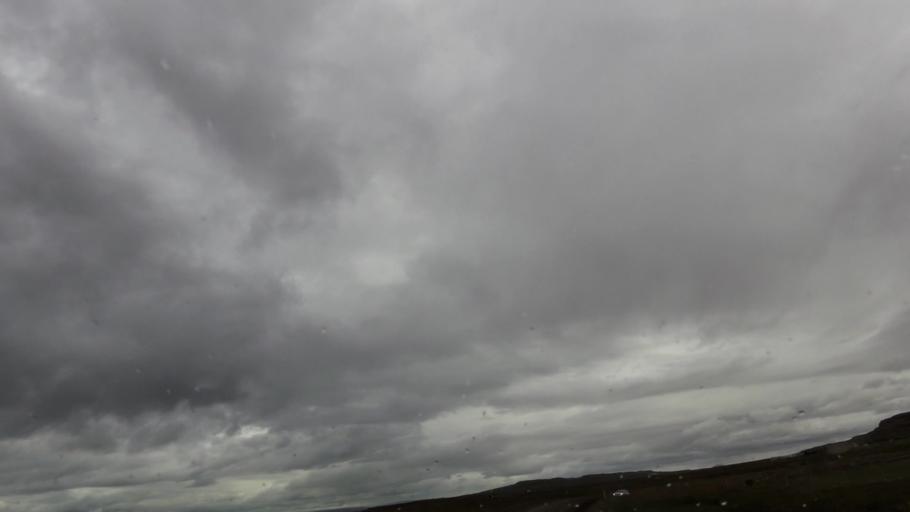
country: IS
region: West
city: Borgarnes
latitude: 65.0253
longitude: -22.1137
